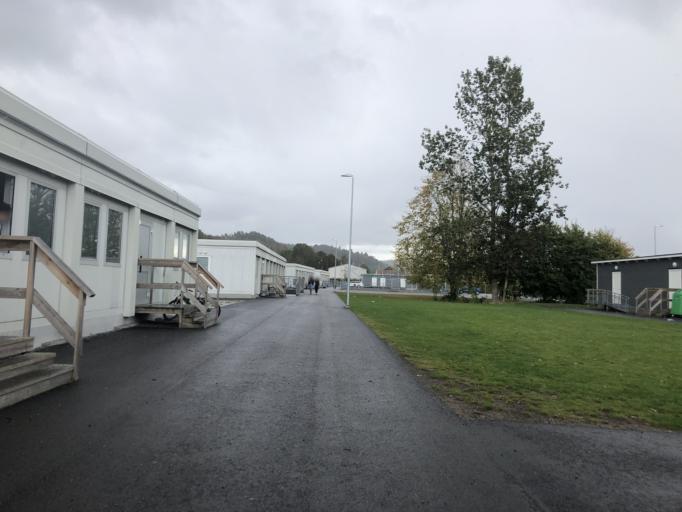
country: SE
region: Vaestra Goetaland
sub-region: Molndal
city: Moelndal
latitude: 57.6515
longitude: 12.0259
